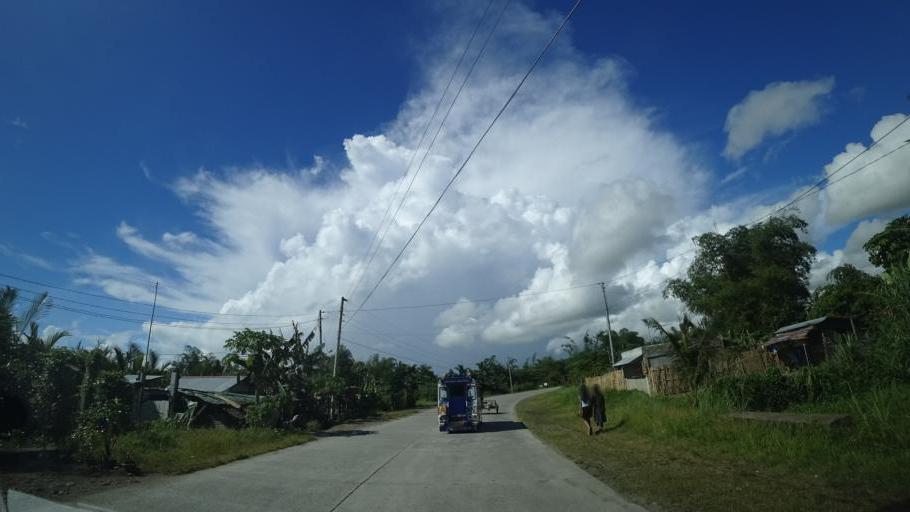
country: PH
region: Eastern Visayas
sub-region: Province of Leyte
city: Palo
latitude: 11.1549
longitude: 125.0016
